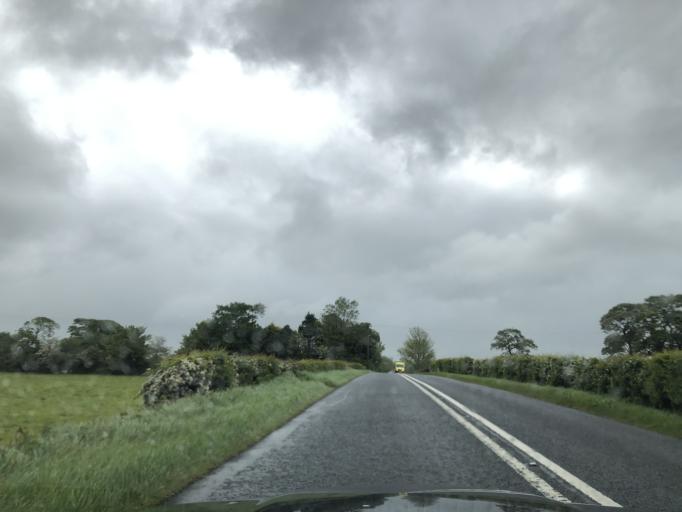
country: GB
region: Northern Ireland
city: Bushmills
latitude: 55.1513
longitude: -6.4298
